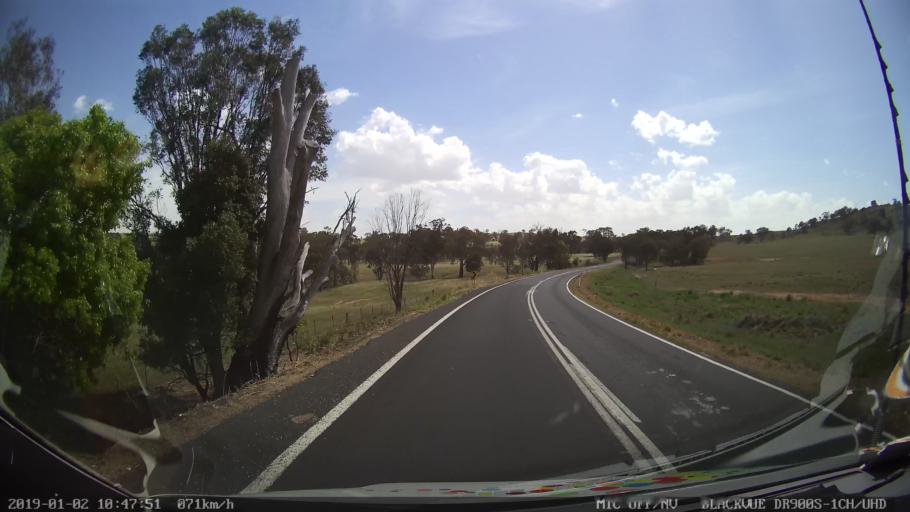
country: AU
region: New South Wales
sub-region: Cootamundra
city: Cootamundra
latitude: -34.7409
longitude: 148.2726
